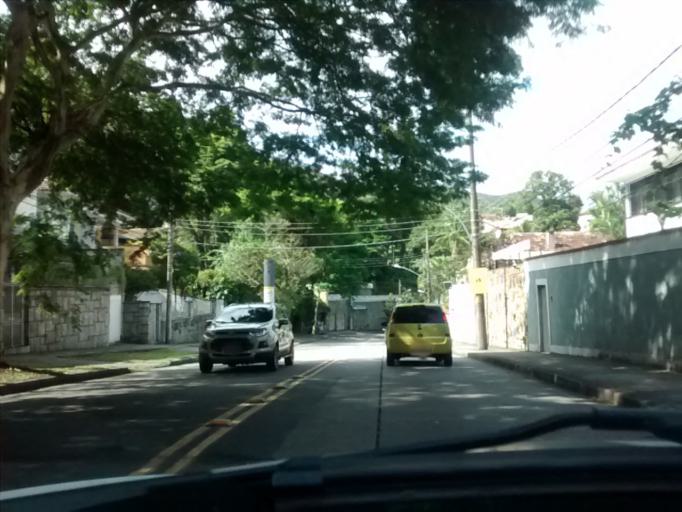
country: BR
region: Rio de Janeiro
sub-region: Rio De Janeiro
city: Rio de Janeiro
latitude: -22.9502
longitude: -43.2619
